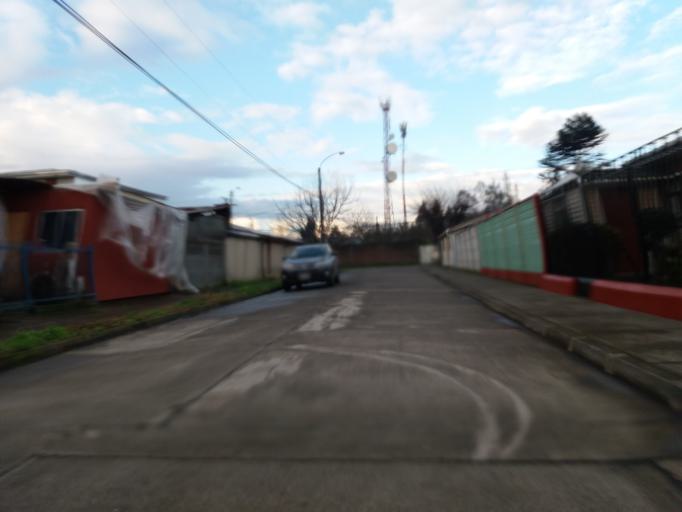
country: CL
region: Araucania
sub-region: Provincia de Cautin
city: Temuco
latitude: -38.7495
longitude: -72.6060
